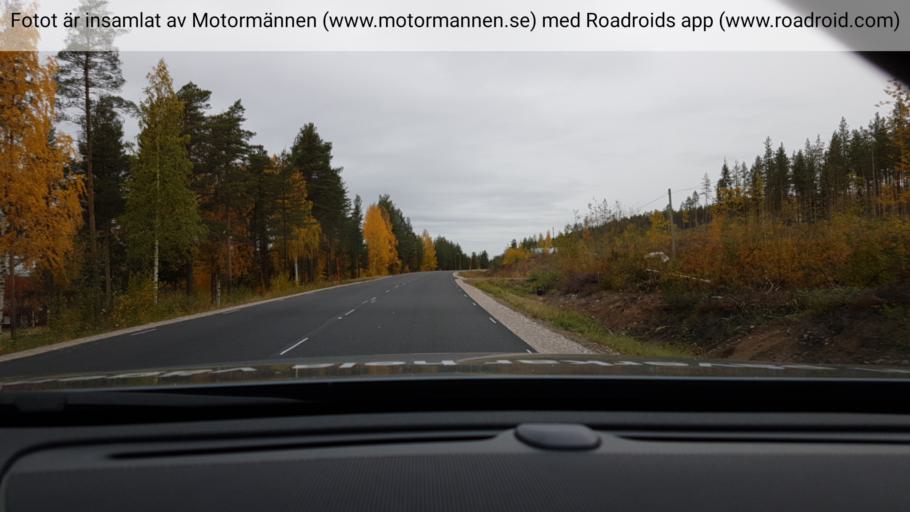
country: SE
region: Norrbotten
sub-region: Overkalix Kommun
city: OEverkalix
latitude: 66.3892
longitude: 22.8220
